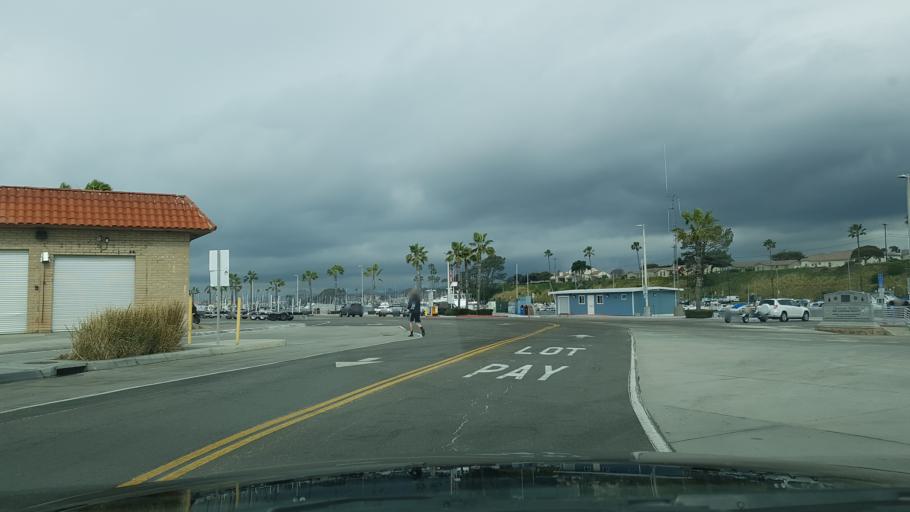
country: US
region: California
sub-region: San Diego County
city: Oceanside
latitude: 33.2050
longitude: -117.3934
